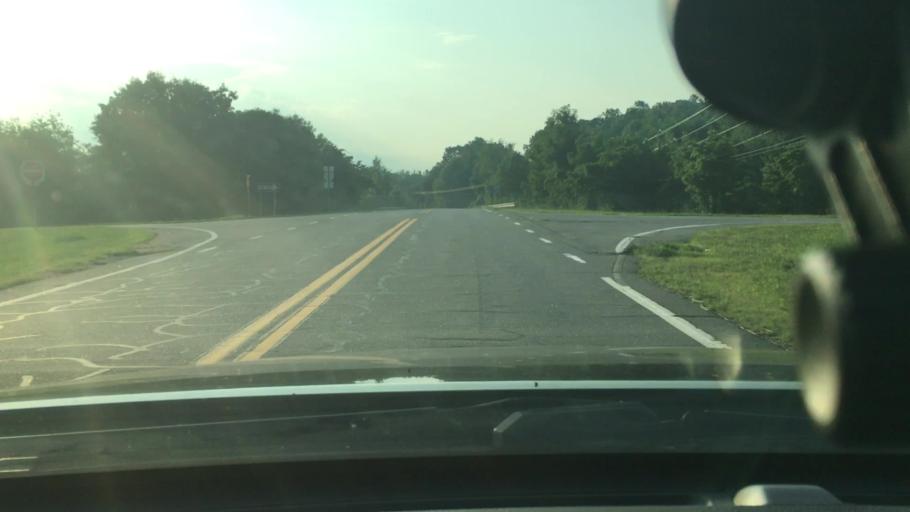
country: US
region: North Carolina
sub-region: McDowell County
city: West Marion
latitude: 35.6328
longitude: -82.0004
